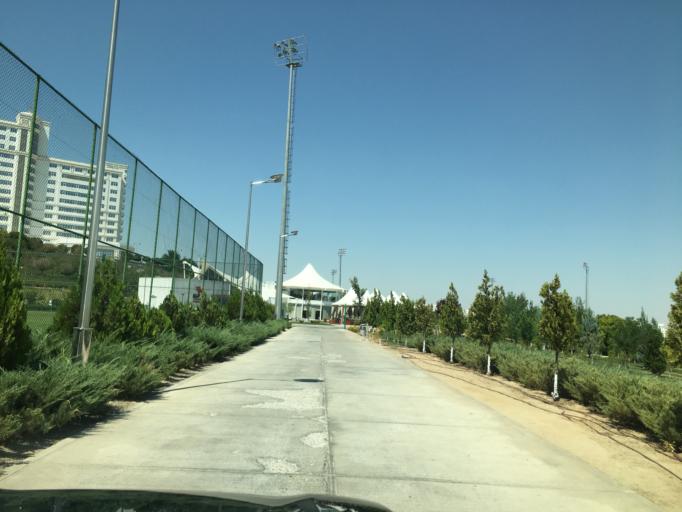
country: TM
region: Ahal
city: Ashgabat
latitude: 37.9273
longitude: 58.3471
